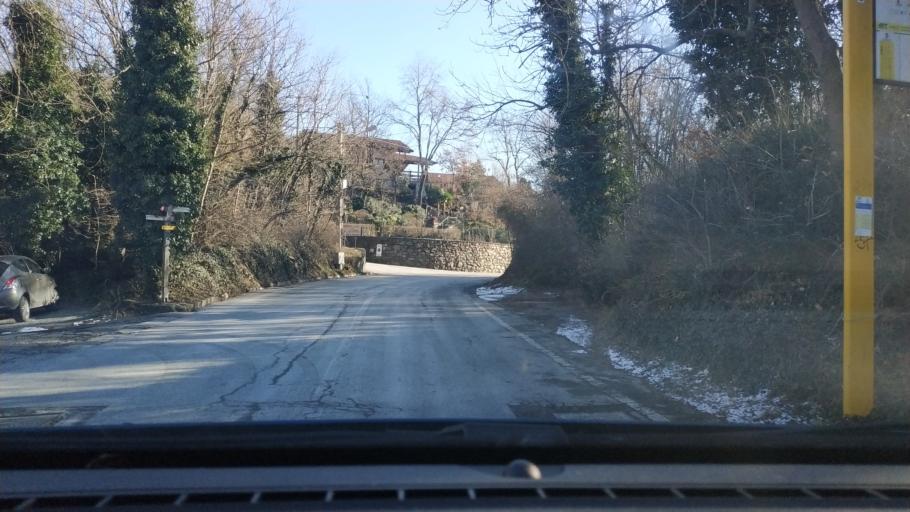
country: IT
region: Piedmont
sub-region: Provincia di Torino
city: Cascinette d'Ivrea
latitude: 45.4814
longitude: 7.8912
